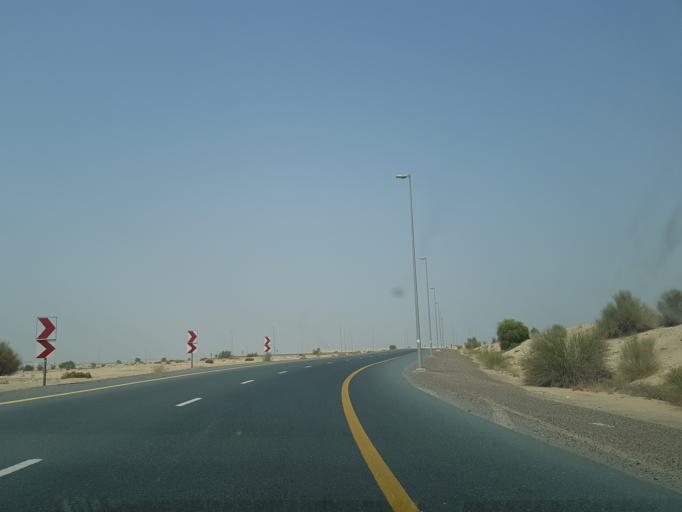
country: AE
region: Dubai
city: Dubai
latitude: 25.0515
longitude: 55.3101
